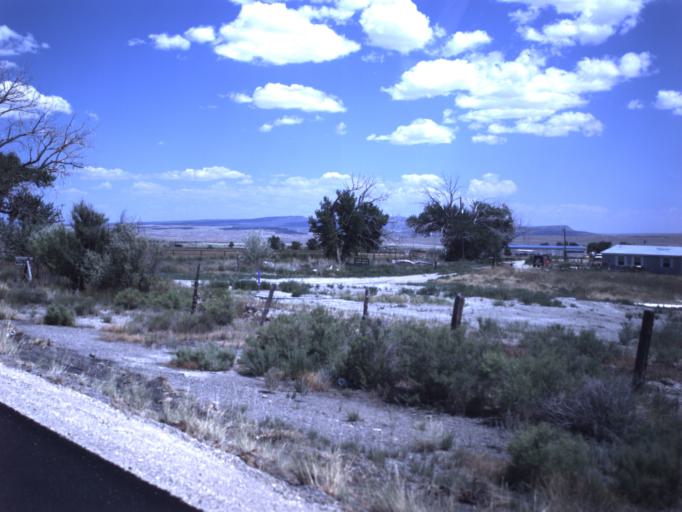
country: US
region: Utah
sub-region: Emery County
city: Castle Dale
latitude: 39.2412
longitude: -110.9979
